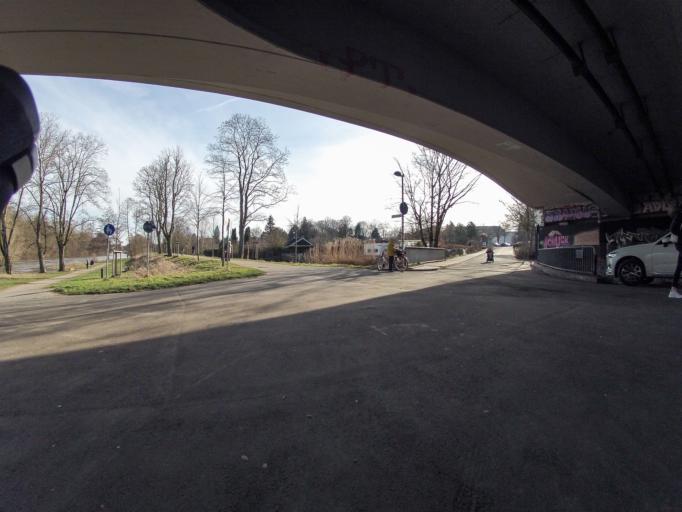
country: DE
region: North Rhine-Westphalia
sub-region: Regierungsbezirk Munster
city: Rheine
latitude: 52.2850
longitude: 7.4339
